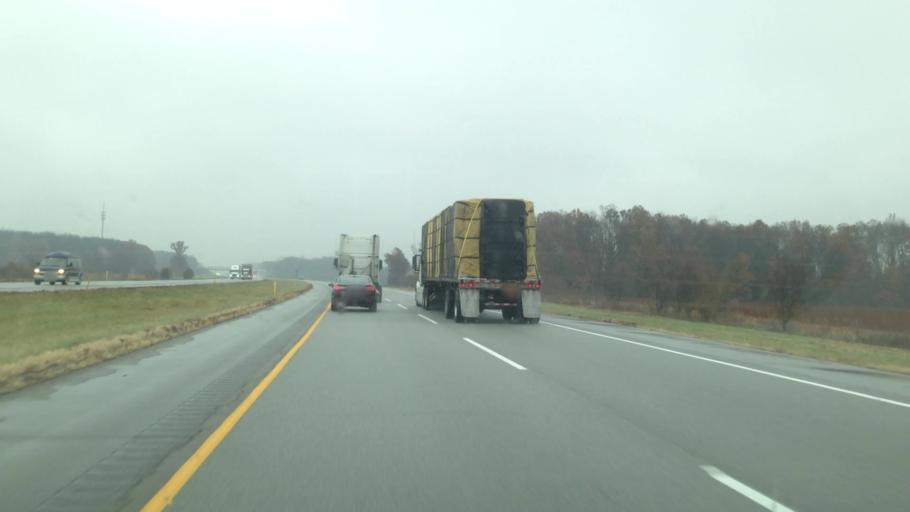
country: US
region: Indiana
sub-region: Saint Joseph County
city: Granger
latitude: 41.7317
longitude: -86.0938
